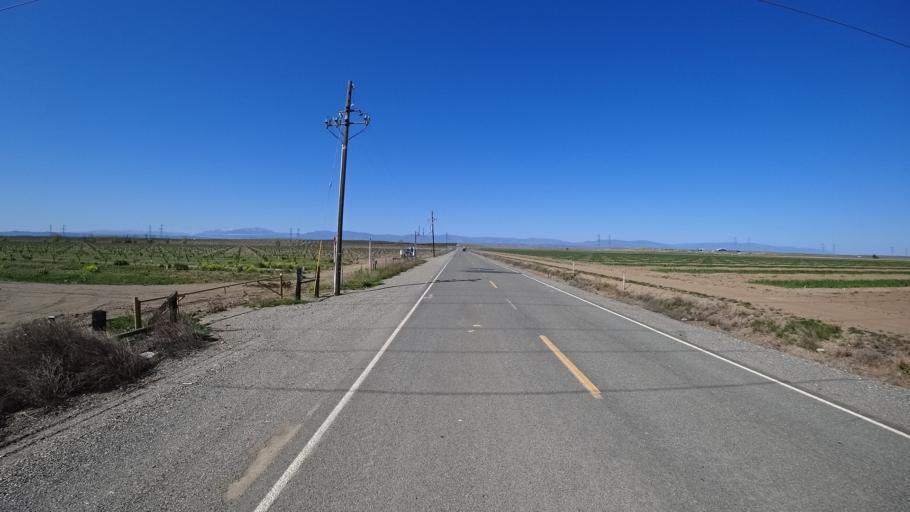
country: US
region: California
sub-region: Glenn County
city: Willows
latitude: 39.6248
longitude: -122.2647
